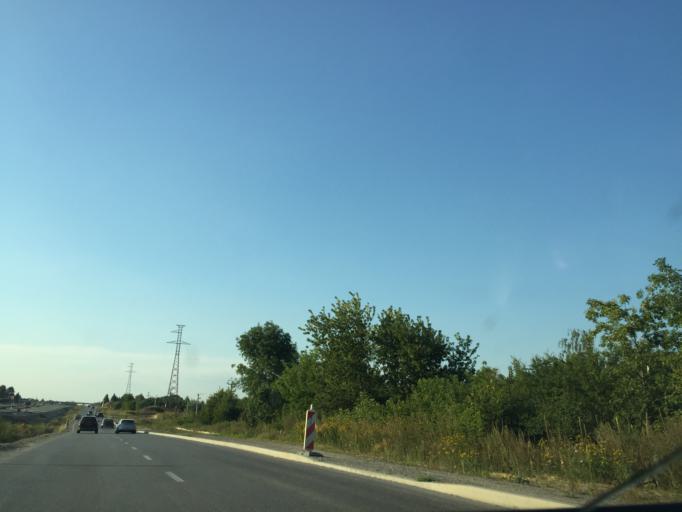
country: PL
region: Masovian Voivodeship
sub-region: Powiat piaseczynski
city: Tarczyn
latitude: 51.9229
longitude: 20.8525
